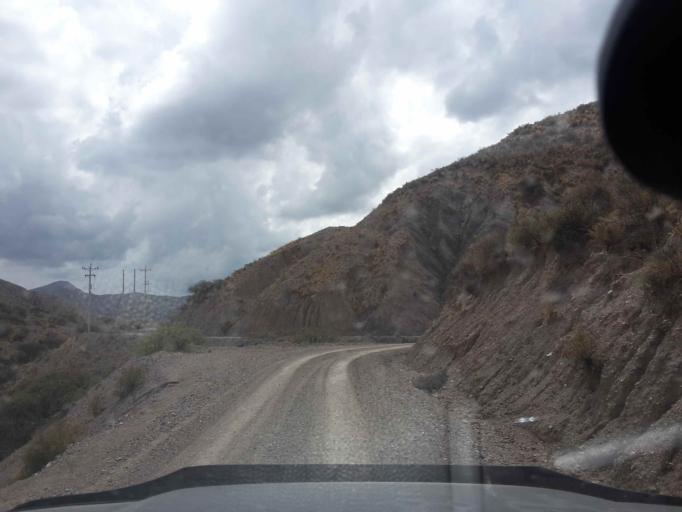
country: BO
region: Cochabamba
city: Colchani
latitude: -17.5152
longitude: -66.6031
